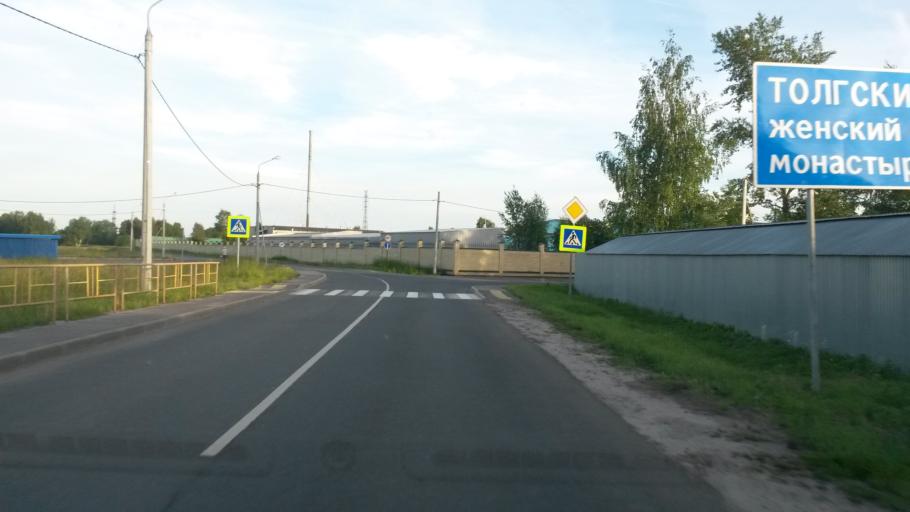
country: RU
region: Jaroslavl
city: Yaroslavl
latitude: 57.7008
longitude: 39.8309
